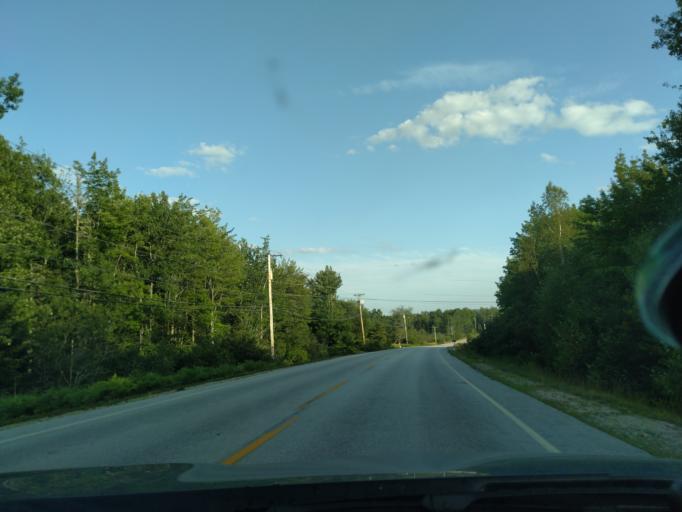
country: US
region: Maine
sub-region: Hancock County
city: Gouldsboro
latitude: 44.4108
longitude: -68.0899
